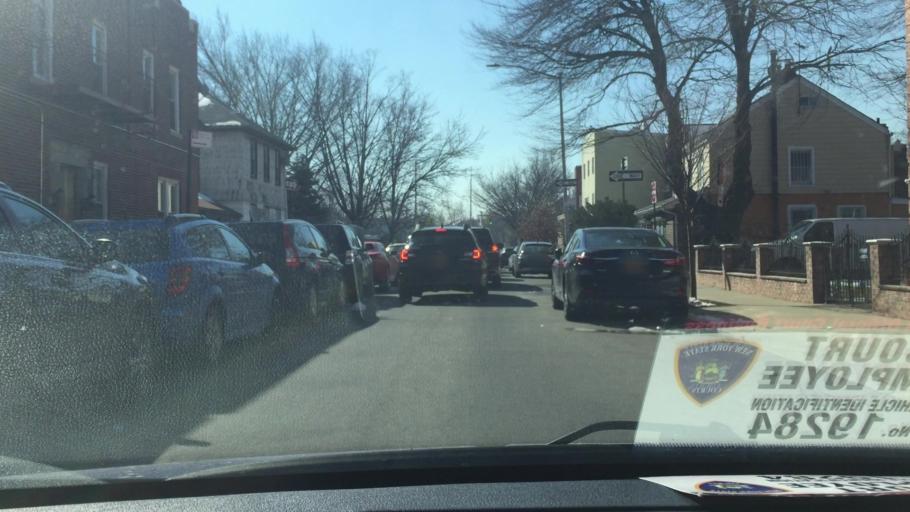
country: US
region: New York
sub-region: Queens County
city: Long Island City
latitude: 40.7699
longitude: -73.9067
